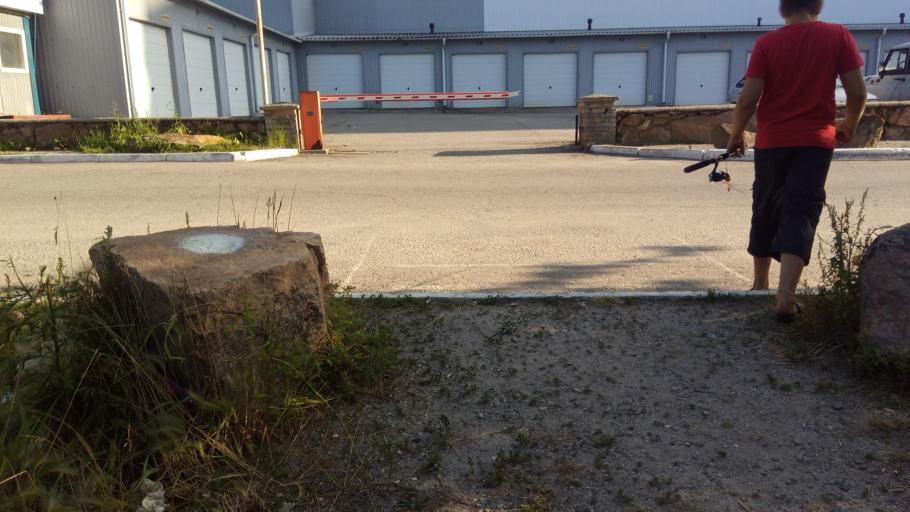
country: RU
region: Chelyabinsk
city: Chebarkul'
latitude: 55.0214
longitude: 60.3133
